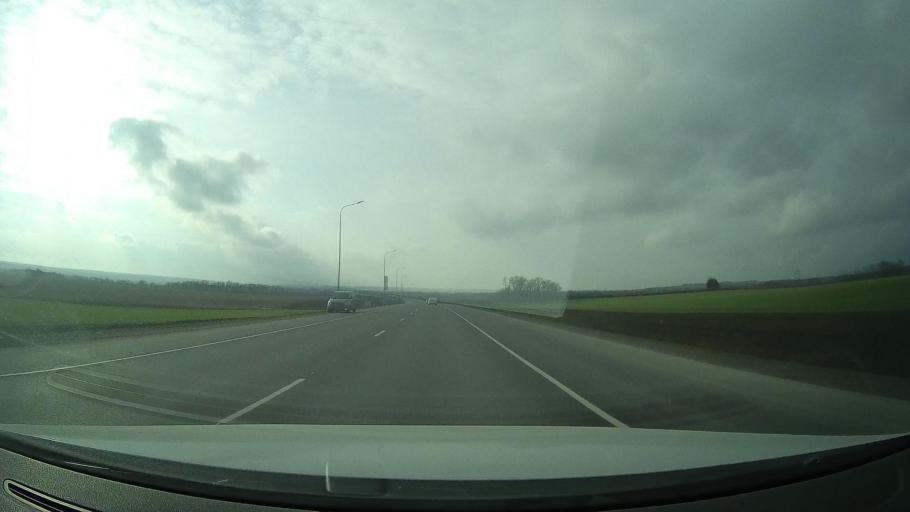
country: RU
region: Rostov
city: Grushevskaya
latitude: 47.4672
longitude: 39.8968
